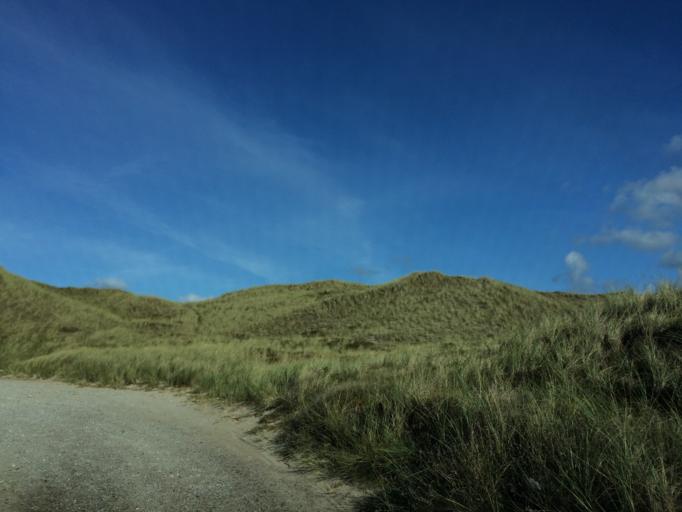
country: DK
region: Central Jutland
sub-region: Holstebro Kommune
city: Ulfborg
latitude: 56.2897
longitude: 8.1288
